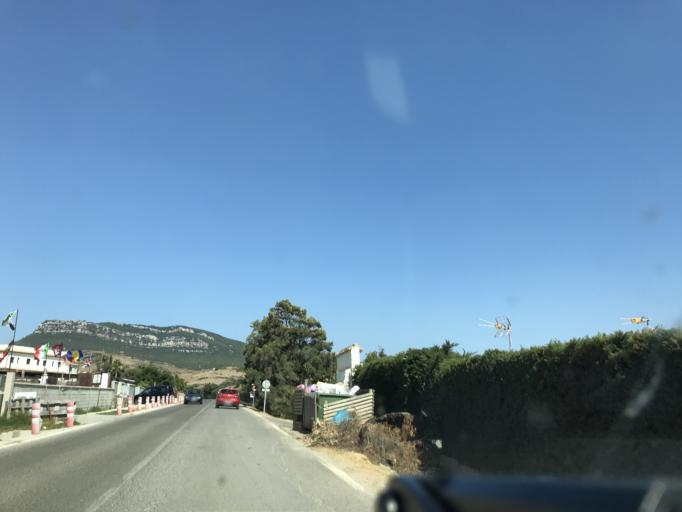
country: ES
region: Andalusia
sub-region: Provincia de Cadiz
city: Zahara de los Atunes
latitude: 36.0878
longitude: -5.7659
